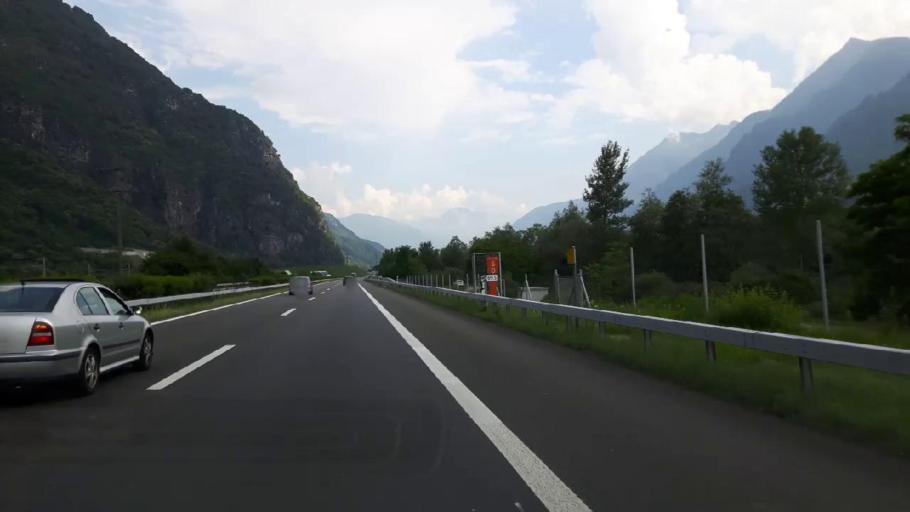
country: CH
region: Ticino
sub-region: Riviera District
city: Biasca
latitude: 46.3321
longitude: 8.9758
